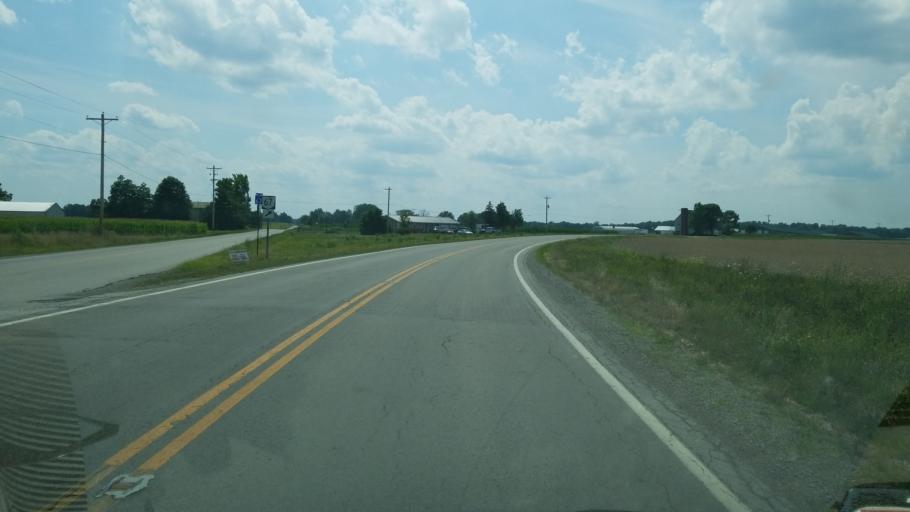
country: US
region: Ohio
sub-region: Hardin County
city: Forest
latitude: 40.6962
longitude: -83.4008
